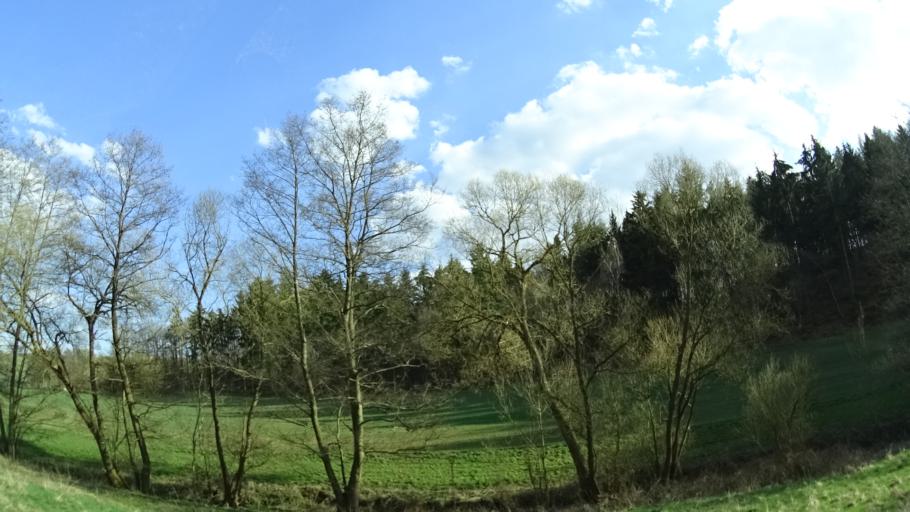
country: DE
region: Rheinland-Pfalz
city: Lauschied
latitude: 49.7480
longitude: 7.6145
